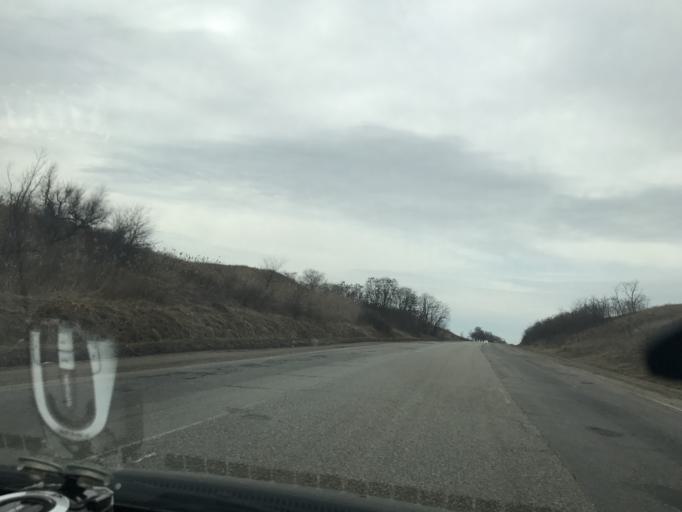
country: RU
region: Krasnodarskiy
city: Zavetnyy
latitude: 44.9180
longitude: 41.1420
